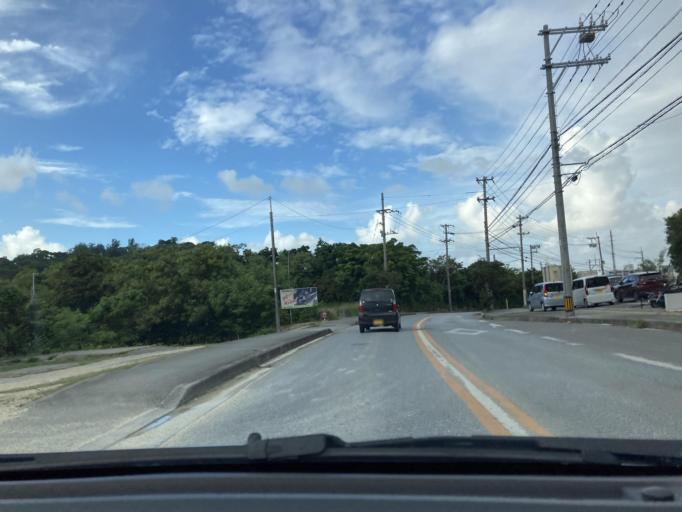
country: JP
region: Okinawa
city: Tomigusuku
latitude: 26.1822
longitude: 127.6852
